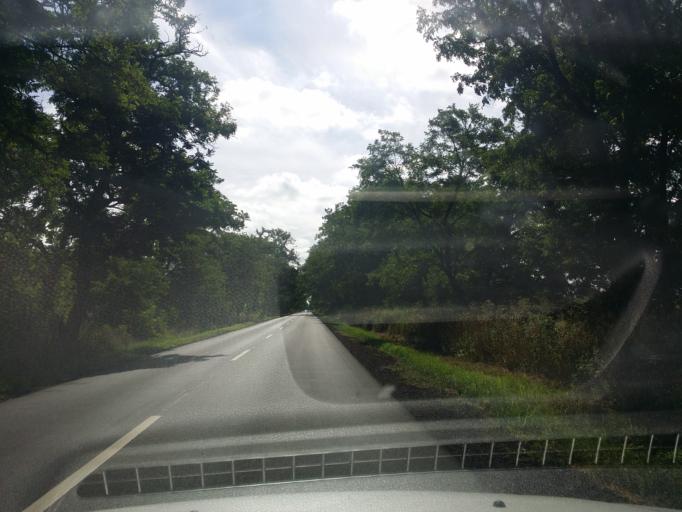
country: HU
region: Heves
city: Heves
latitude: 47.6244
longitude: 20.2474
